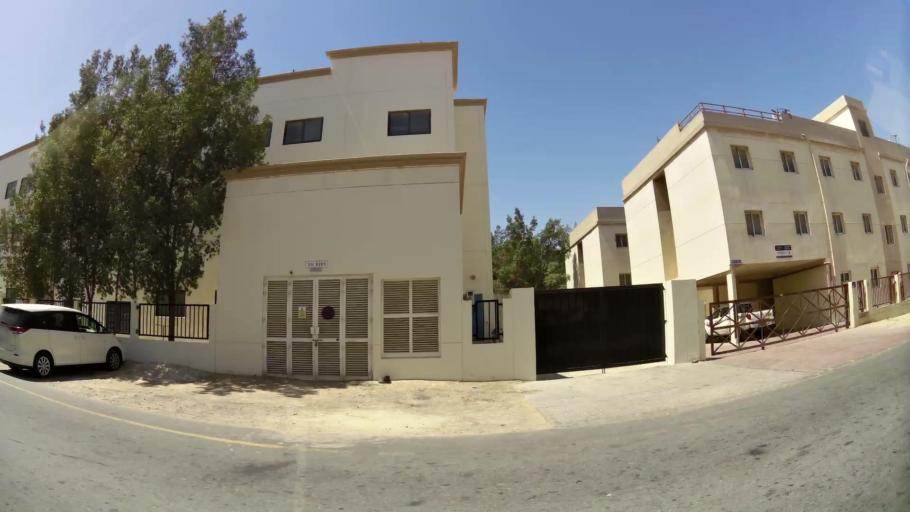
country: AE
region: Dubai
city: Dubai
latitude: 24.9902
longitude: 55.1980
